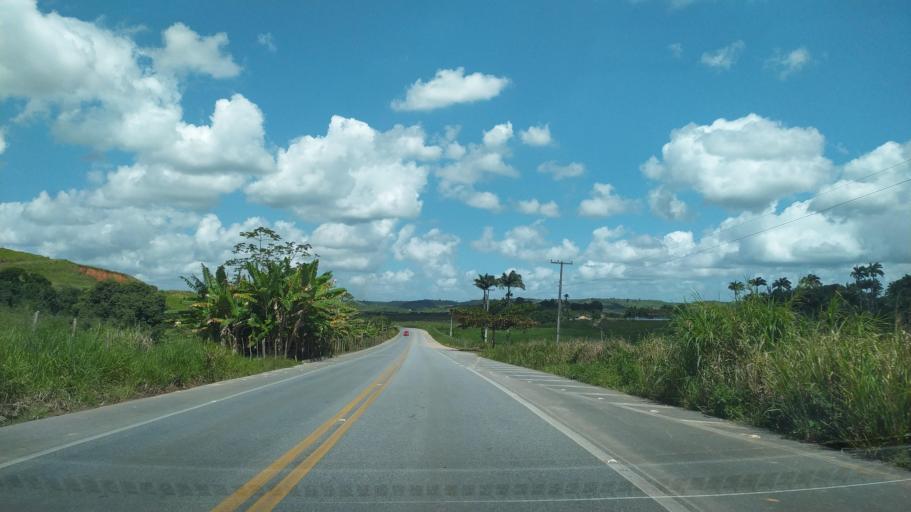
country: BR
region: Alagoas
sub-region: Murici
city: Murici
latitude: -9.2873
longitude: -35.9623
